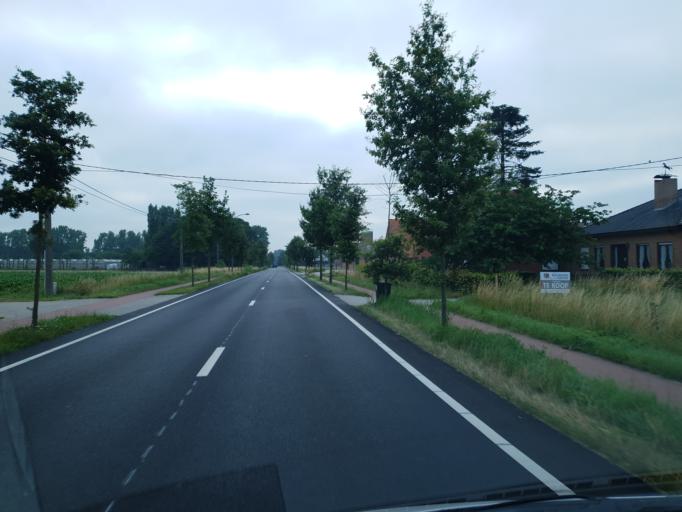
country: BE
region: Flanders
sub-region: Provincie Antwerpen
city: Brecht
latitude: 51.3604
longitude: 4.6995
